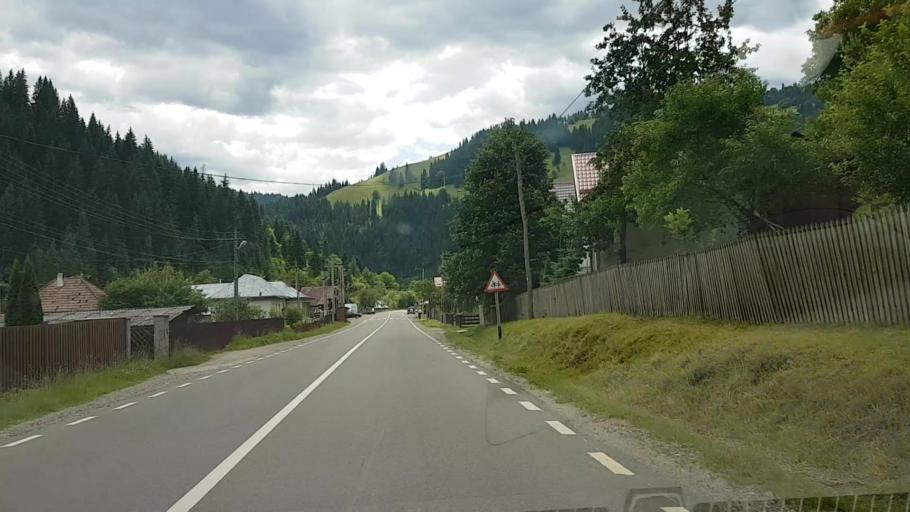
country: RO
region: Neamt
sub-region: Comuna Farcasa
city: Farcasa
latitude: 47.1473
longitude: 25.8645
